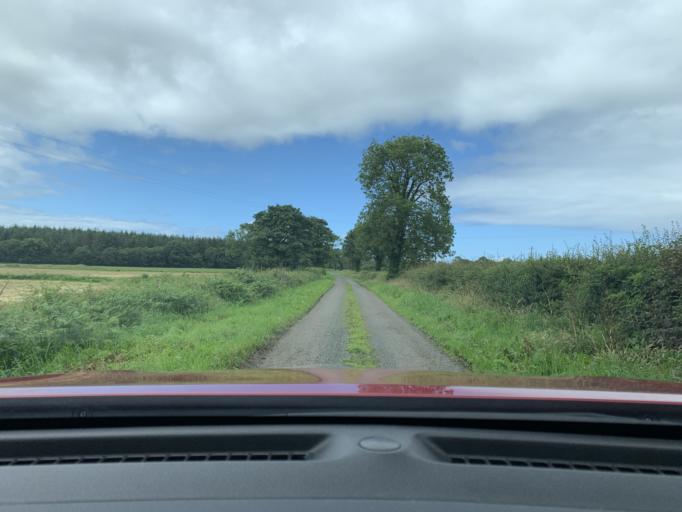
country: IE
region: Connaught
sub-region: Sligo
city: Sligo
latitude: 54.3310
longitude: -8.4825
